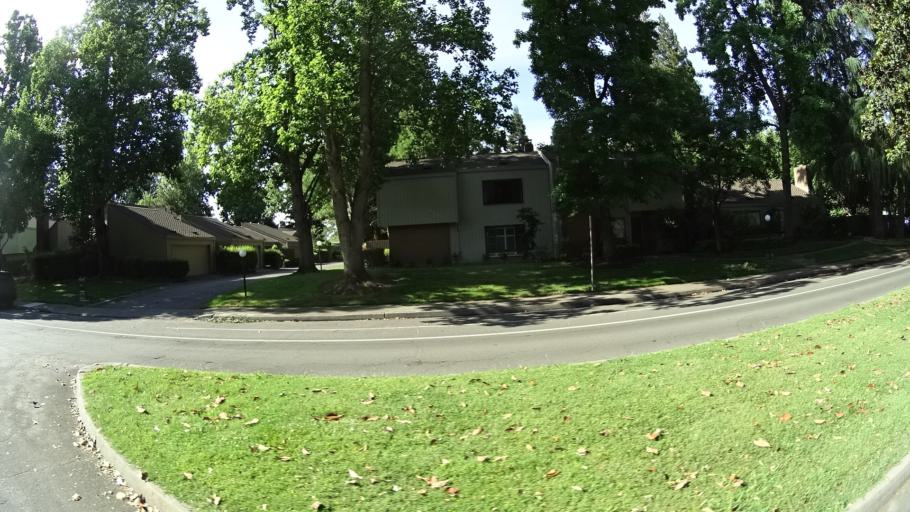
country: US
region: California
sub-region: Sacramento County
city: Rosemont
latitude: 38.5617
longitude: -121.4130
